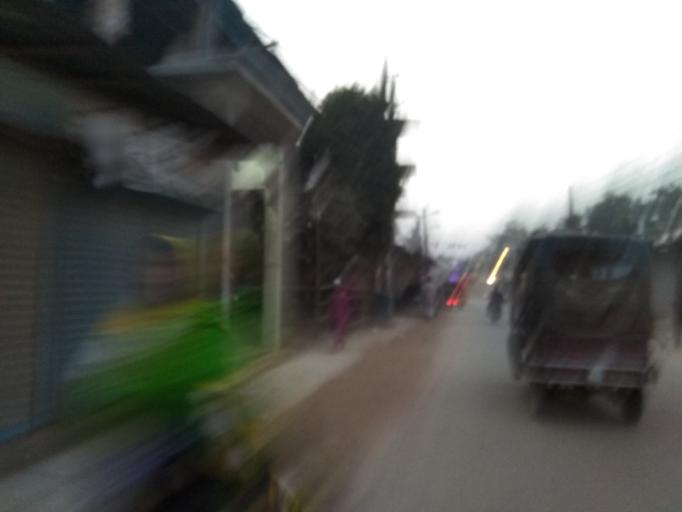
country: BD
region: Rangpur Division
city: Rangpur
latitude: 25.7407
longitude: 89.2532
